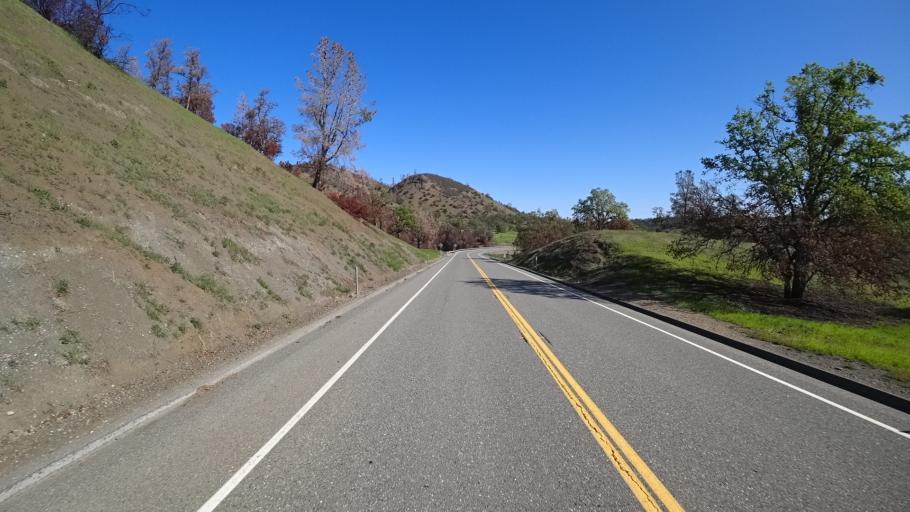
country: US
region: California
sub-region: Glenn County
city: Orland
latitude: 39.6539
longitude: -122.5937
